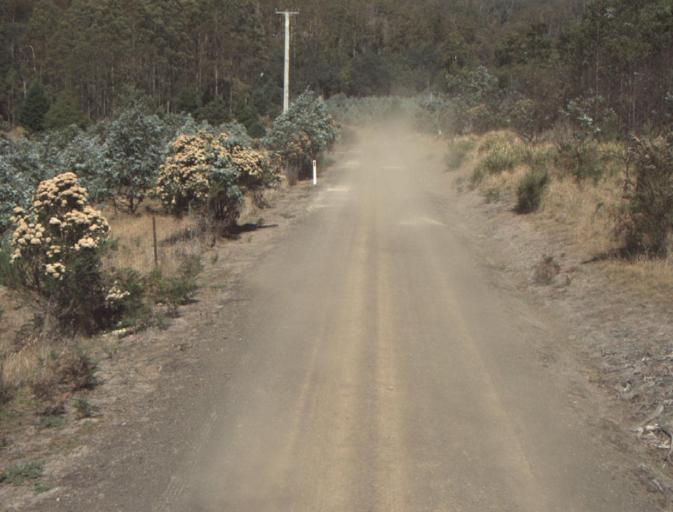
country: AU
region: Tasmania
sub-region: Dorset
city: Scottsdale
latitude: -41.3172
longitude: 147.3826
